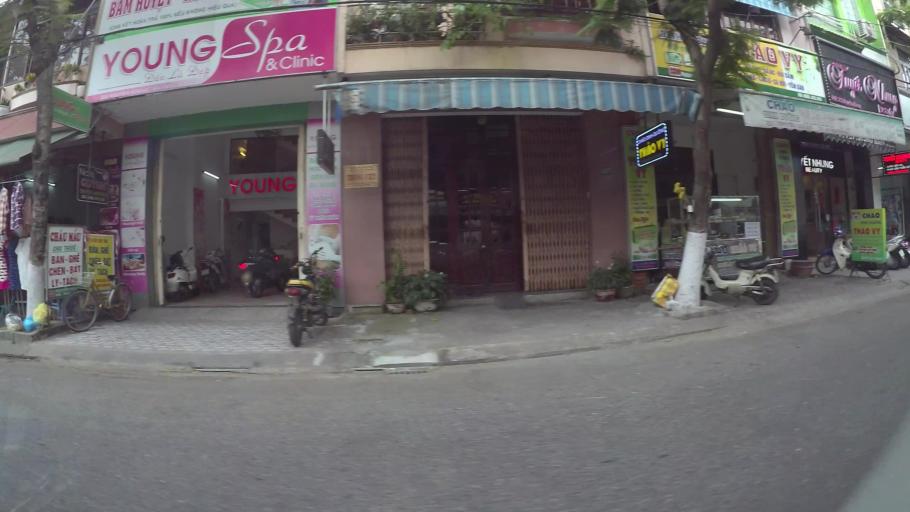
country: VN
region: Da Nang
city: Da Nang
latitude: 16.0583
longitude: 108.2132
